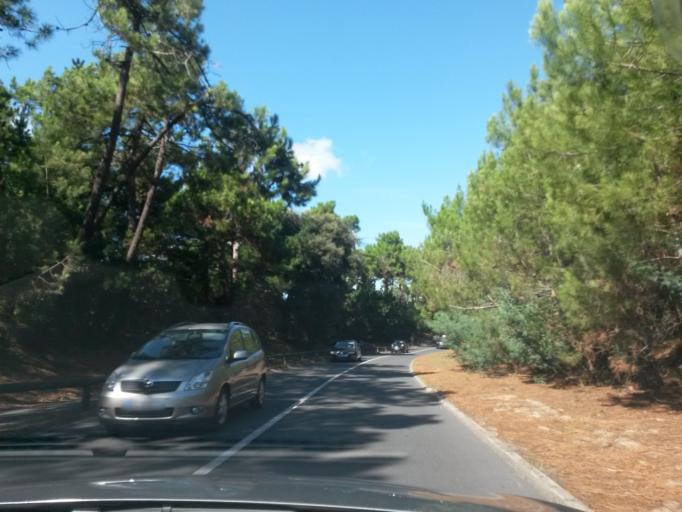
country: FR
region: Aquitaine
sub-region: Departement de la Gironde
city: Arcachon
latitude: 44.6906
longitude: -1.2396
